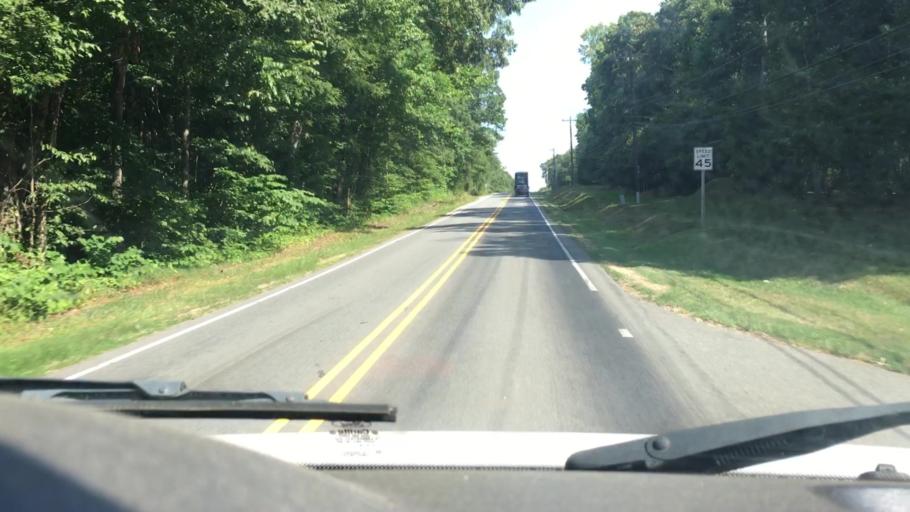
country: US
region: North Carolina
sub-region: Gaston County
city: Davidson
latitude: 35.4612
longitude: -80.8076
